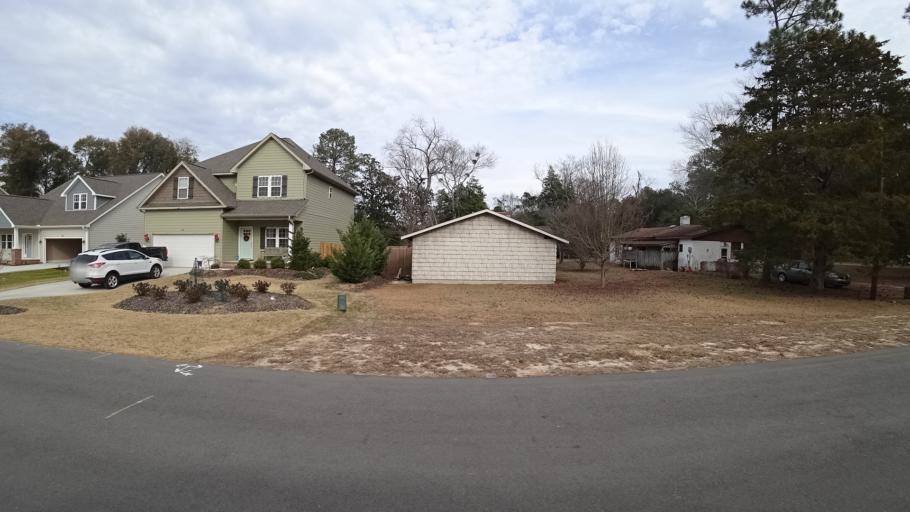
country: US
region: North Carolina
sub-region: Moore County
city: Pinehurst
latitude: 35.2027
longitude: -79.4658
